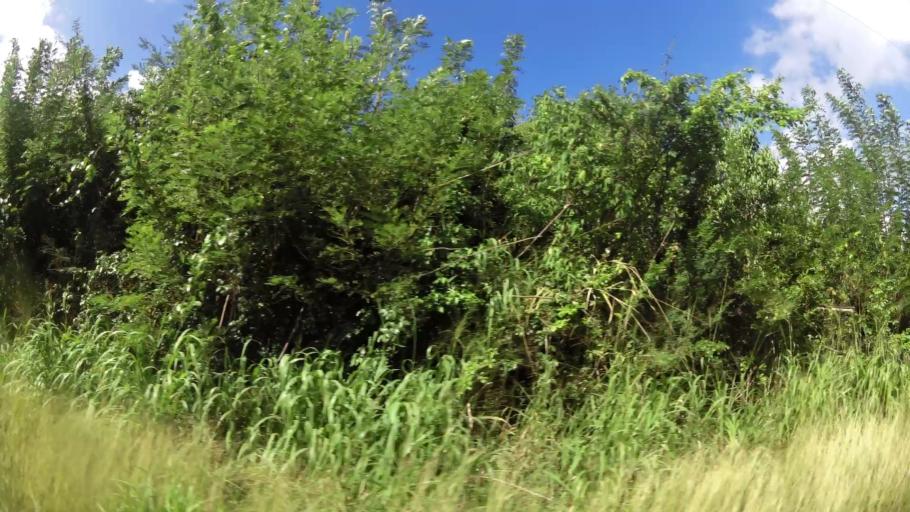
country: MQ
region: Martinique
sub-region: Martinique
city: Le Marin
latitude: 14.4170
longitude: -60.8780
